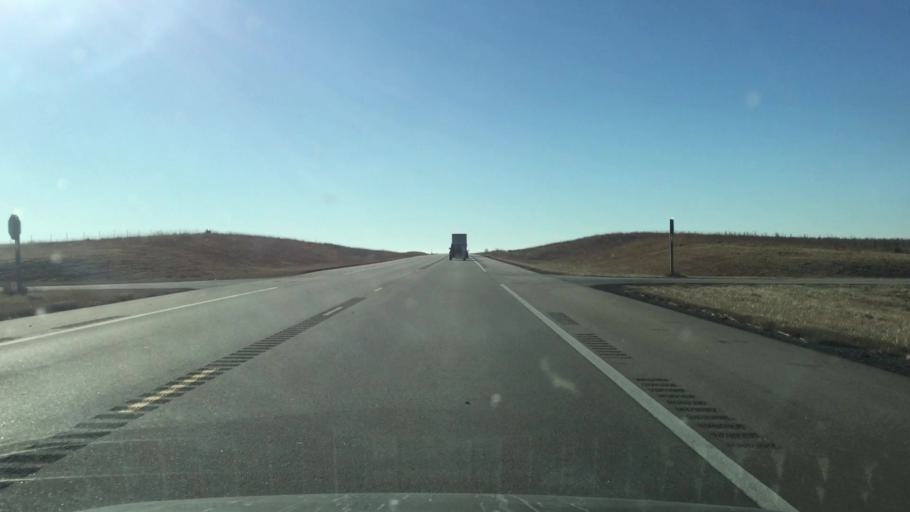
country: US
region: Kansas
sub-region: Allen County
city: Iola
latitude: 38.0532
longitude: -95.3804
